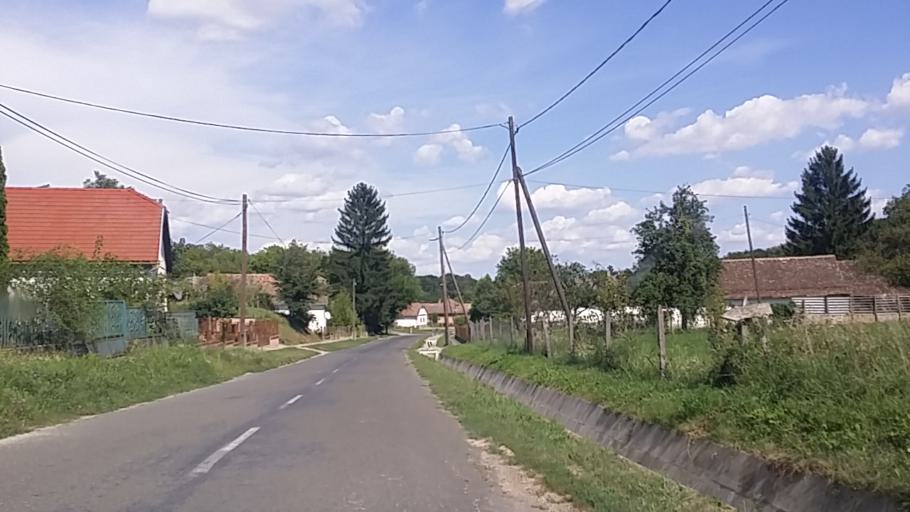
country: HU
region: Tolna
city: Gyonk
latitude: 46.5371
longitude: 18.4661
